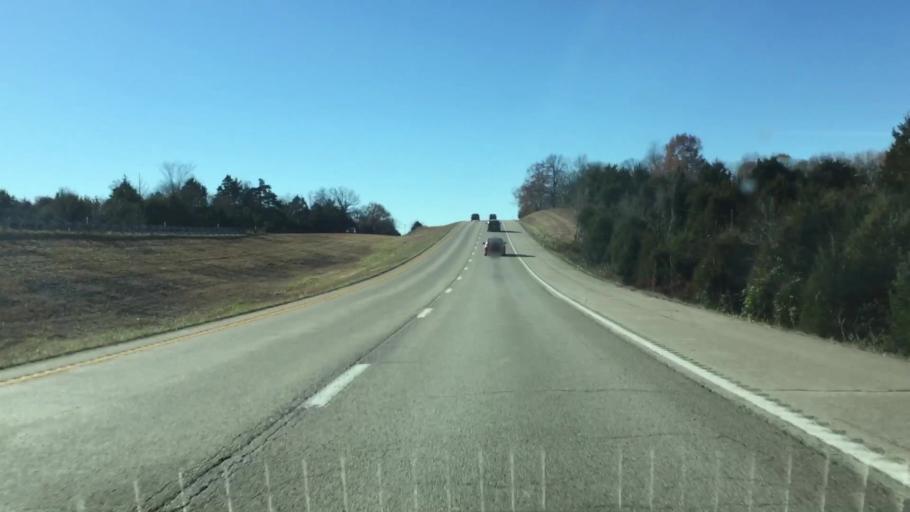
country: US
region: Missouri
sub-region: Cole County
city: Wardsville
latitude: 38.4571
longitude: -92.2983
